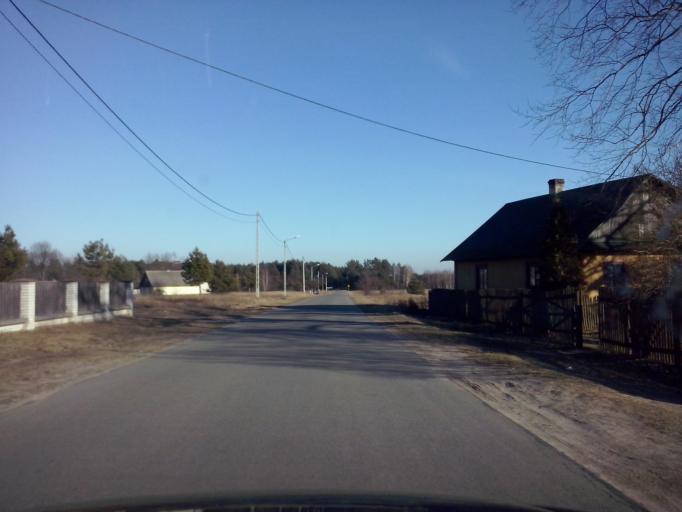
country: PL
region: Subcarpathian Voivodeship
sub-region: Powiat nizanski
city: Harasiuki
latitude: 50.5349
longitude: 22.4721
